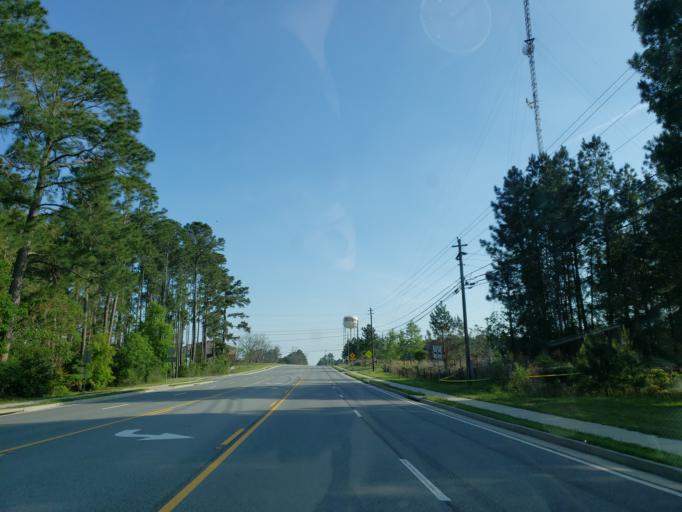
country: US
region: Georgia
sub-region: Tift County
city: Tifton
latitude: 31.4769
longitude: -83.5429
